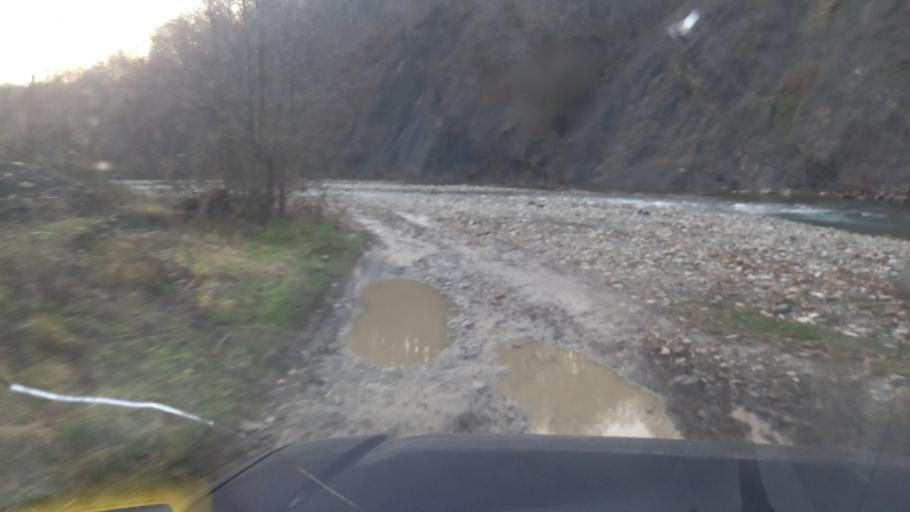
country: RU
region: Krasnodarskiy
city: Goryachiy Klyuch
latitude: 44.3861
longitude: 39.1630
